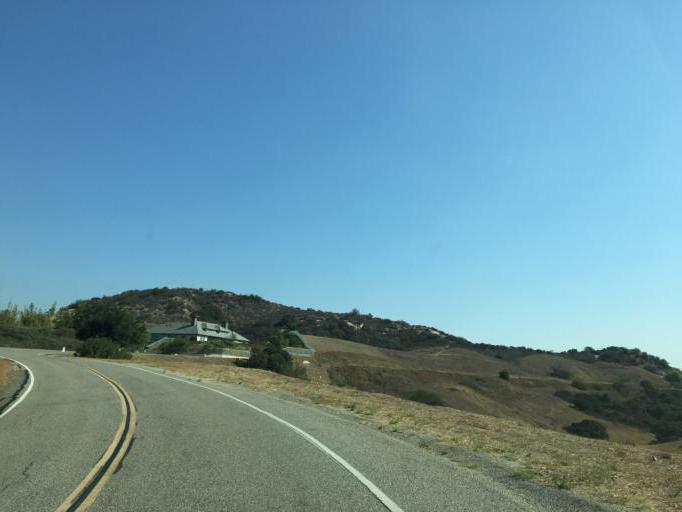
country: US
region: California
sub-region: Los Angeles County
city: Hidden Hills
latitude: 34.1270
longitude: -118.6593
